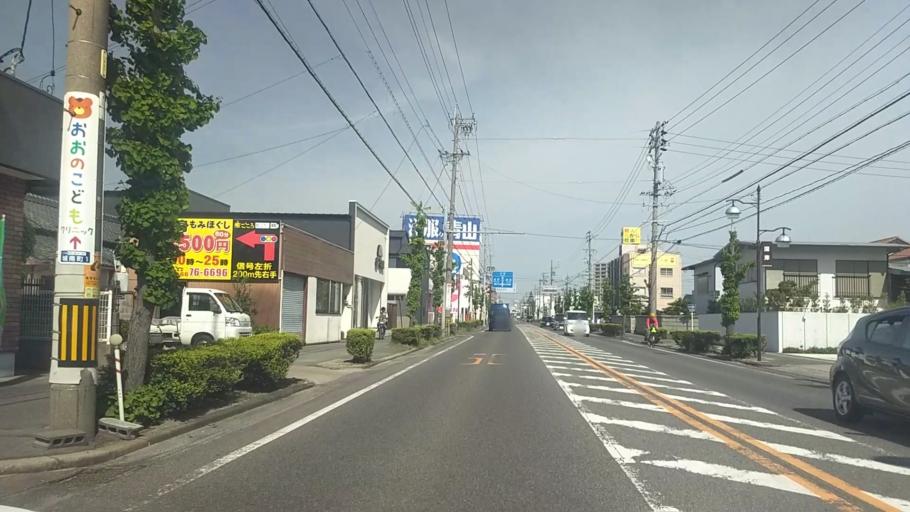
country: JP
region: Aichi
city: Anjo
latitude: 34.9531
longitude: 137.0807
